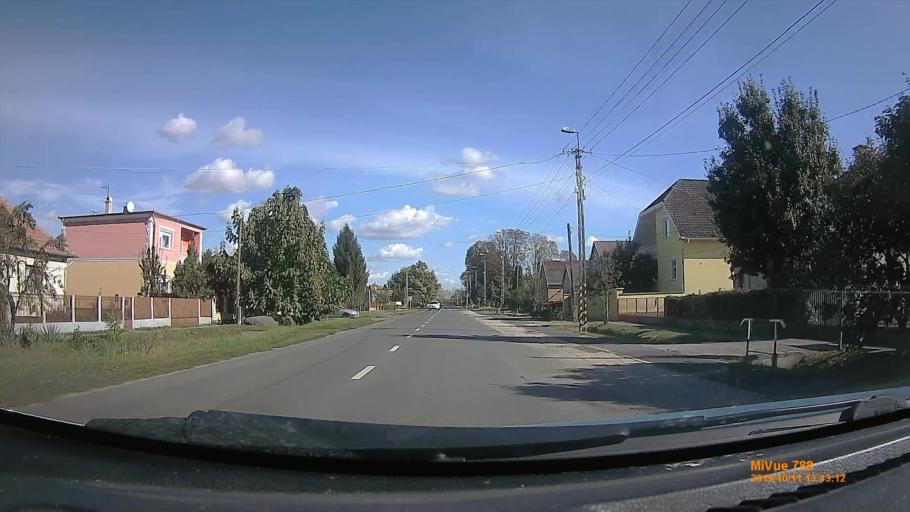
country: HU
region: Hajdu-Bihar
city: Balmazujvaros
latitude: 47.5389
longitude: 21.3498
